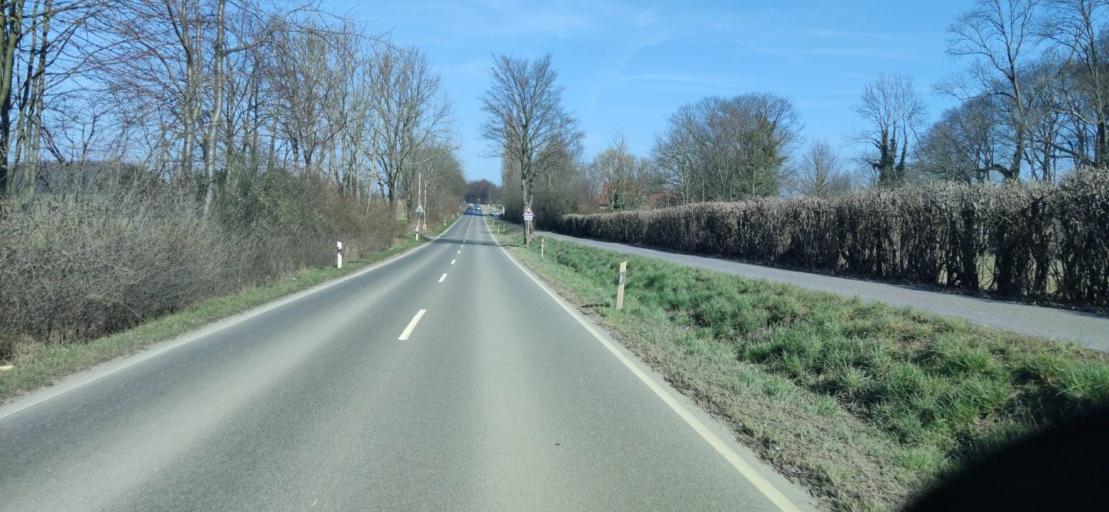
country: DE
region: North Rhine-Westphalia
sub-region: Regierungsbezirk Dusseldorf
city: Erkrath
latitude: 51.2491
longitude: 6.8981
